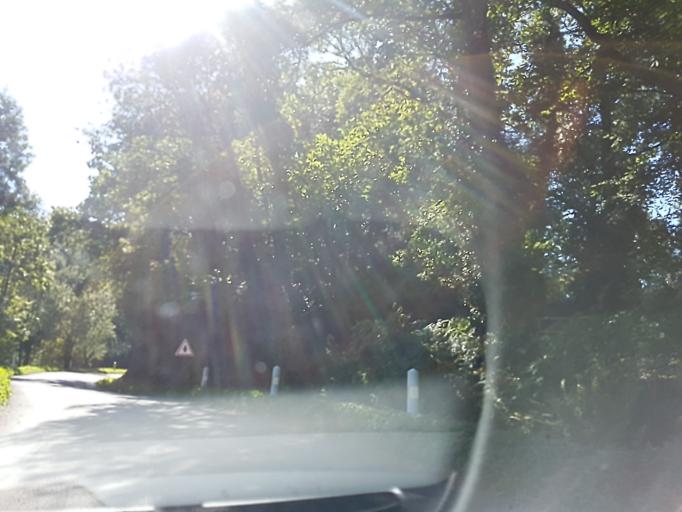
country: FR
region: Brittany
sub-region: Departement du Morbihan
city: Pluherlin
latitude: 47.6953
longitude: -2.3464
